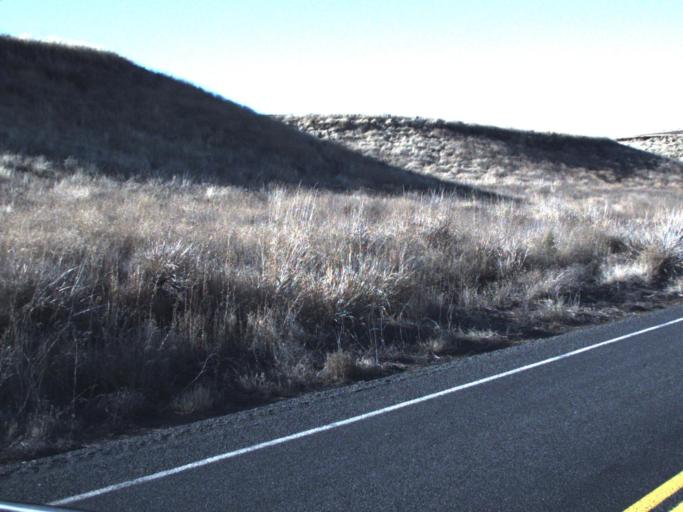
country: US
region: Washington
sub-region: Adams County
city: Ritzville
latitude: 46.8266
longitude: -118.3244
